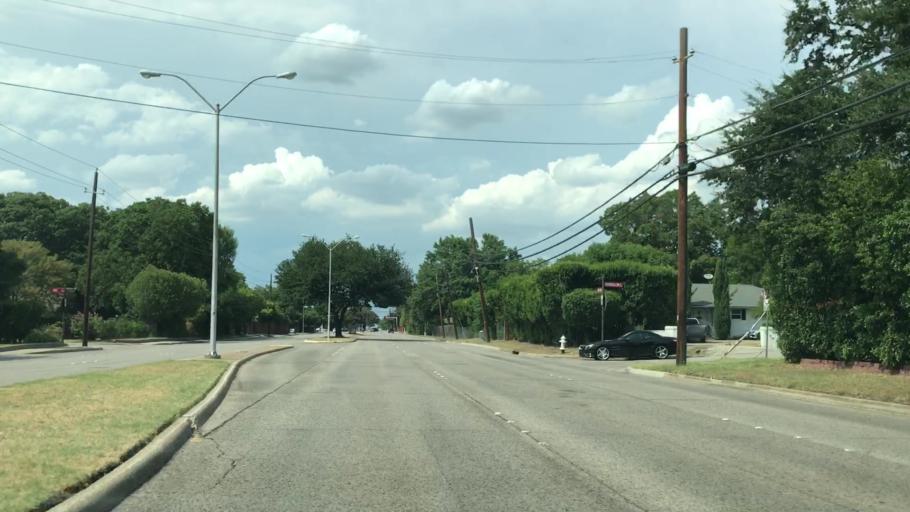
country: US
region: Texas
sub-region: Dallas County
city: Farmers Branch
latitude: 32.9213
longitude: -96.8732
